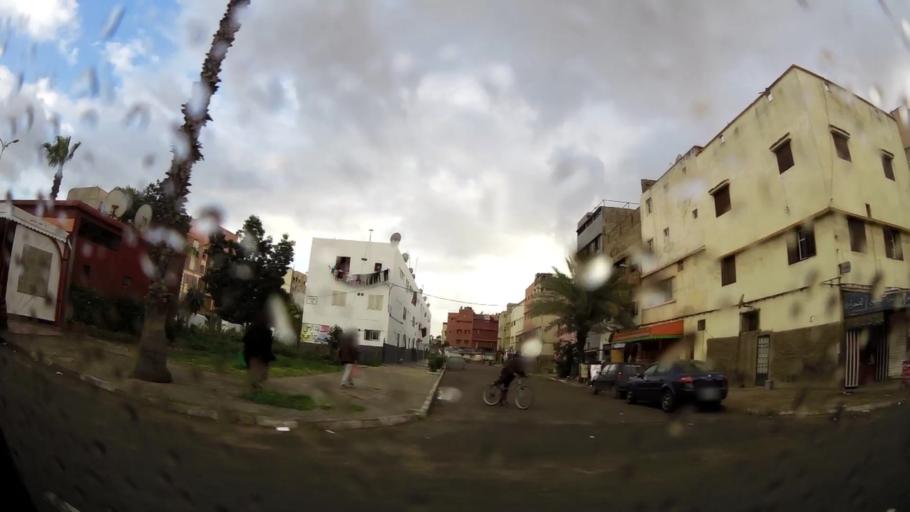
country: MA
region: Grand Casablanca
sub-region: Mohammedia
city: Mohammedia
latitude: 33.6837
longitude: -7.3861
